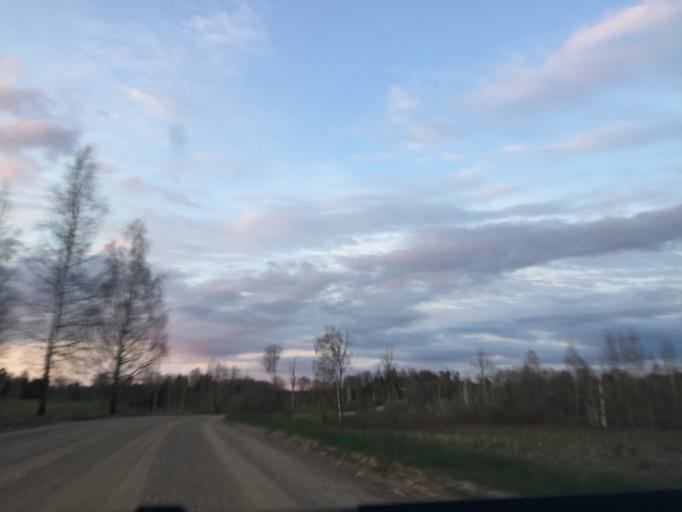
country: LV
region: Aluksnes Rajons
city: Aluksne
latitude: 57.3647
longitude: 26.9940
